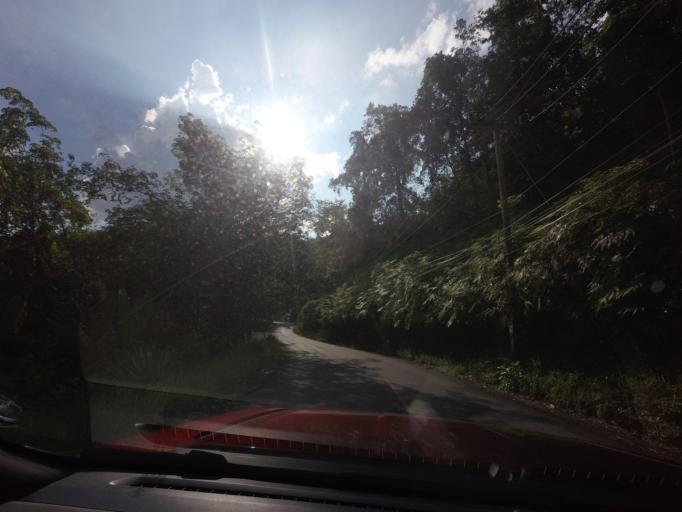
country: TH
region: Yala
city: Than To
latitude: 6.1426
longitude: 101.2892
